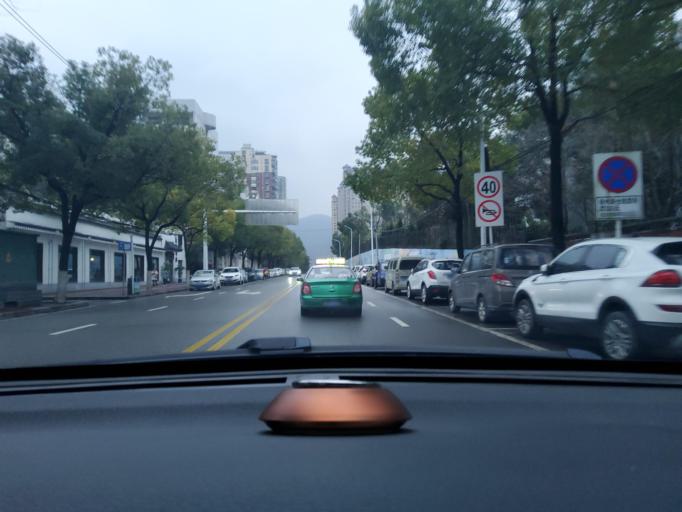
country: CN
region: Hubei
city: Tuanchengshan
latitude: 30.1927
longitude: 115.0275
